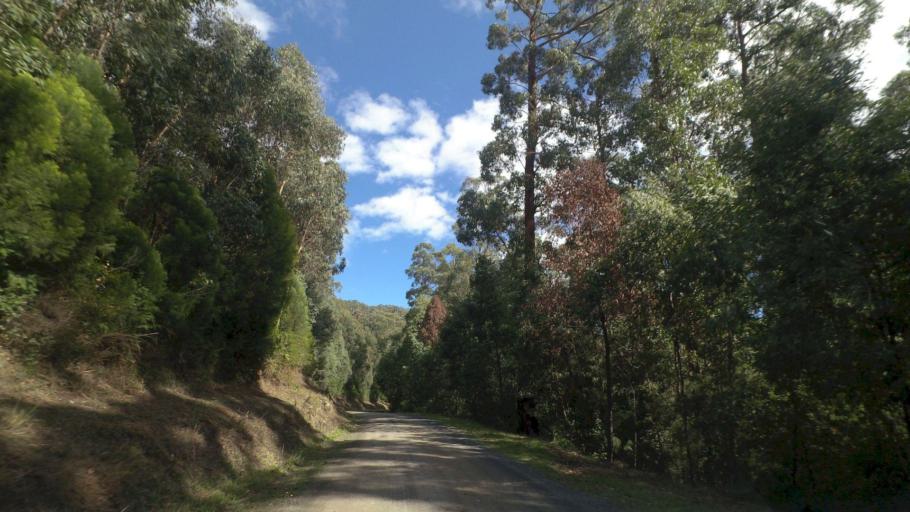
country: AU
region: Victoria
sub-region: Cardinia
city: Bunyip
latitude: -37.9419
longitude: 145.8011
